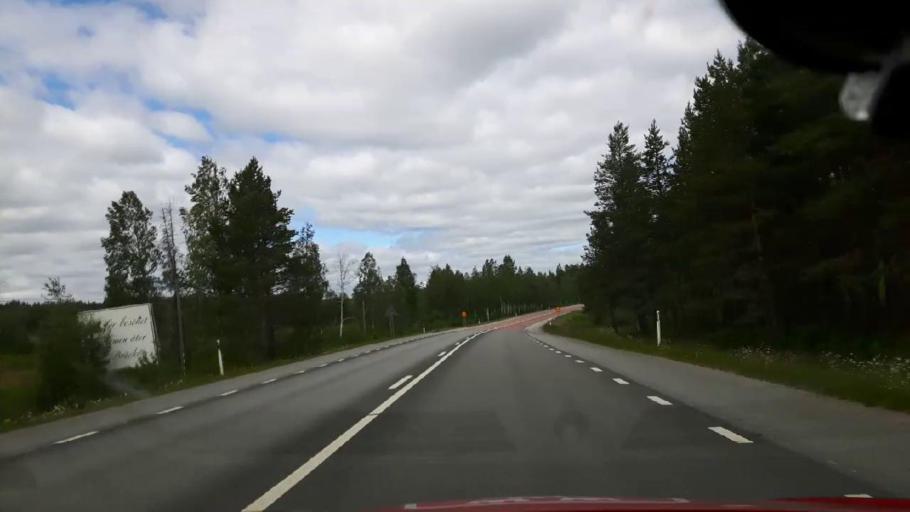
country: SE
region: Jaemtland
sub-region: Braecke Kommun
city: Braecke
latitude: 62.7597
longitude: 15.4098
